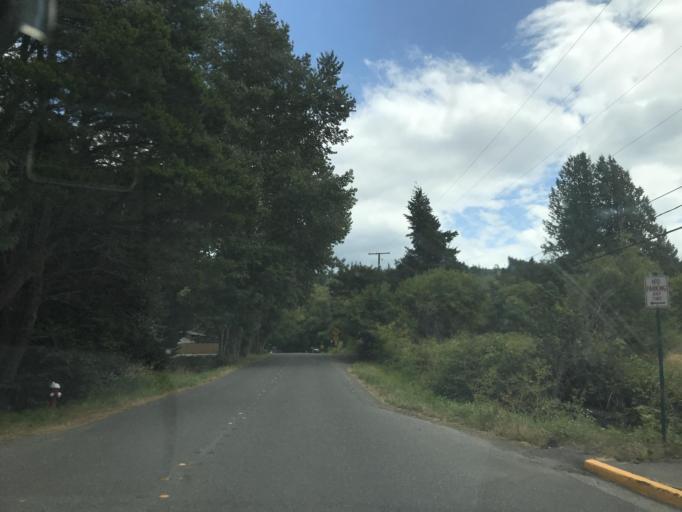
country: US
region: Washington
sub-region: Whatcom County
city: Bellingham
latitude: 48.7240
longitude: -122.4801
